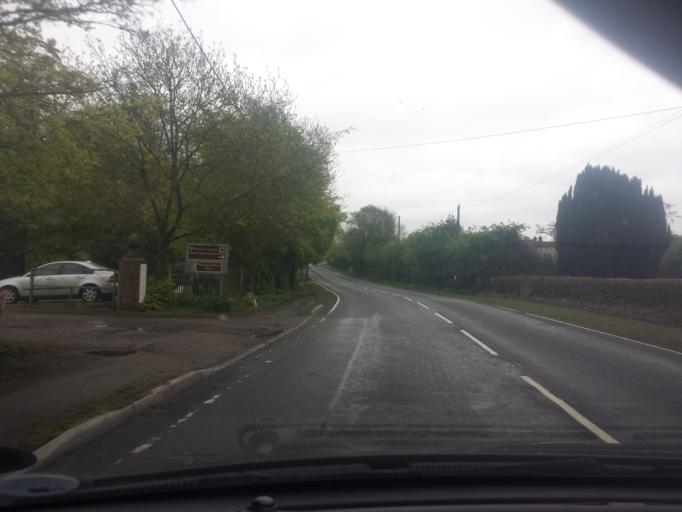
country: GB
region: England
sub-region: Essex
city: Mistley
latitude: 51.9446
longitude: 1.0743
